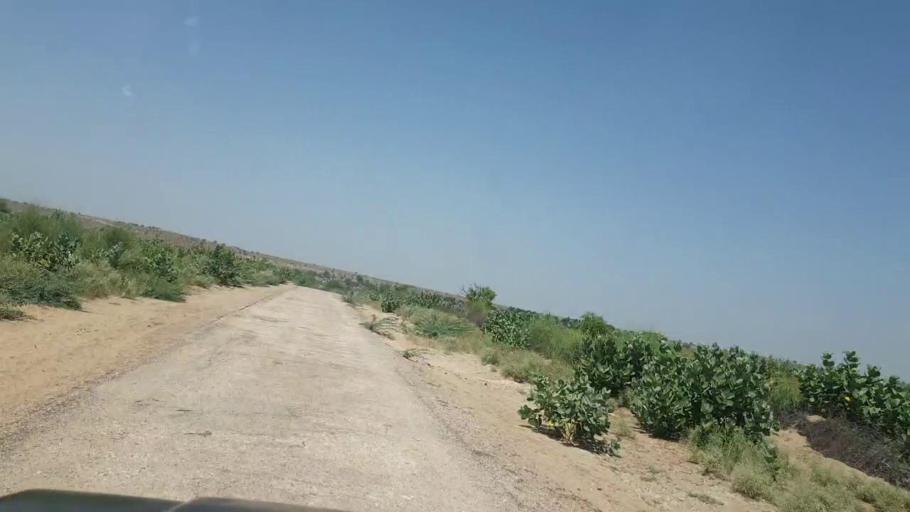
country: PK
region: Sindh
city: Chor
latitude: 25.3702
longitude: 70.3193
